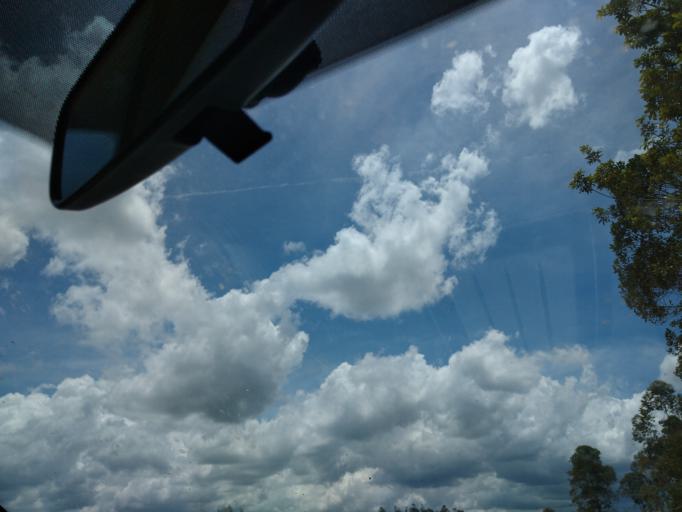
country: BR
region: Minas Gerais
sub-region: Sao Joao Del Rei
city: Sao Joao del Rei
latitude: -20.9003
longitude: -44.2988
